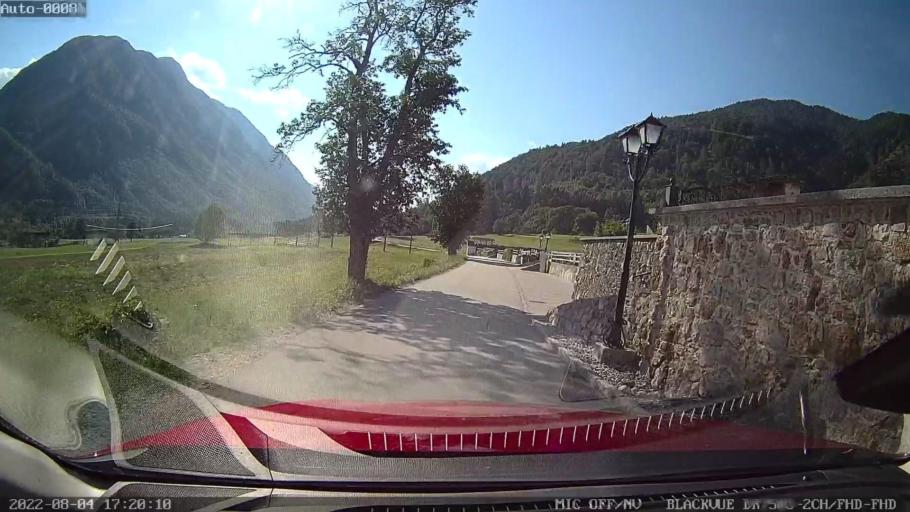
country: SI
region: Jesenice
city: Hrusica
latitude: 46.4673
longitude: 13.9423
